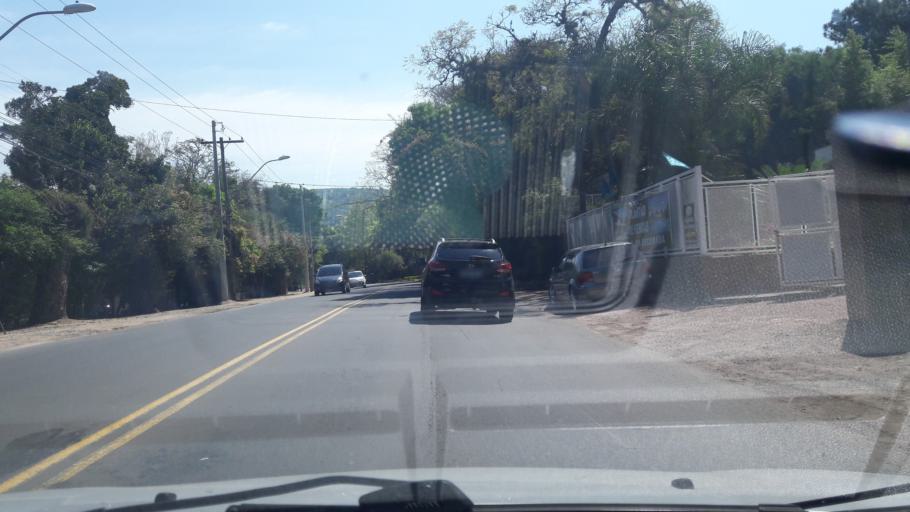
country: BR
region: Rio Grande do Sul
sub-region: Guaiba
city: Guaiba
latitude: -30.1267
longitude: -51.2429
